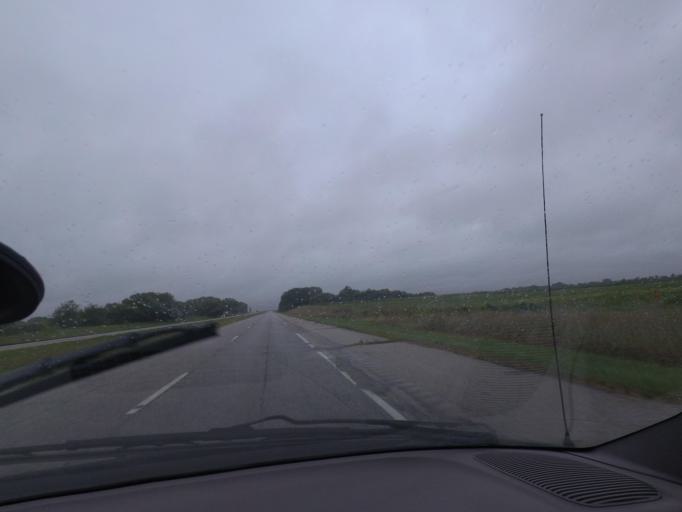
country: US
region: Illinois
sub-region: Pike County
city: Pittsfield
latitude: 39.6702
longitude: -90.8145
